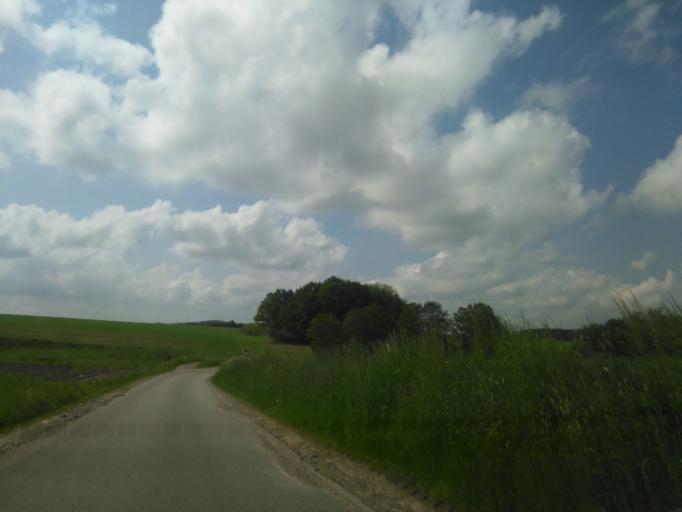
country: DK
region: Central Jutland
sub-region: Arhus Kommune
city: Sabro
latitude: 56.2135
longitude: 9.9764
